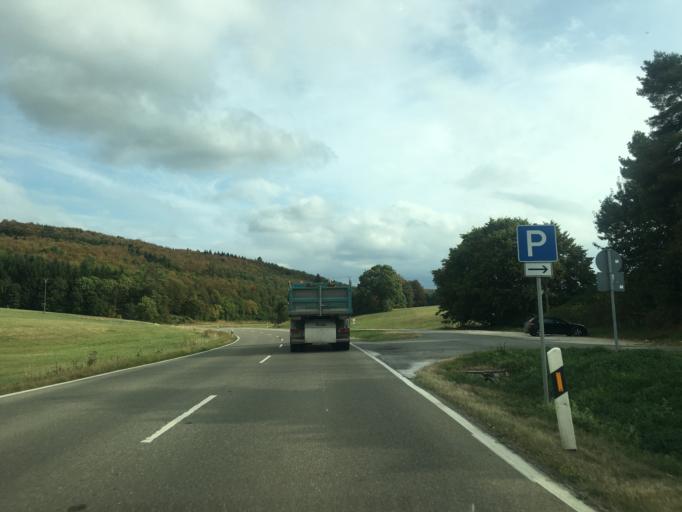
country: DE
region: Baden-Wuerttemberg
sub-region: Tuebingen Region
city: Pfullingen
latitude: 48.4046
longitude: 9.2121
